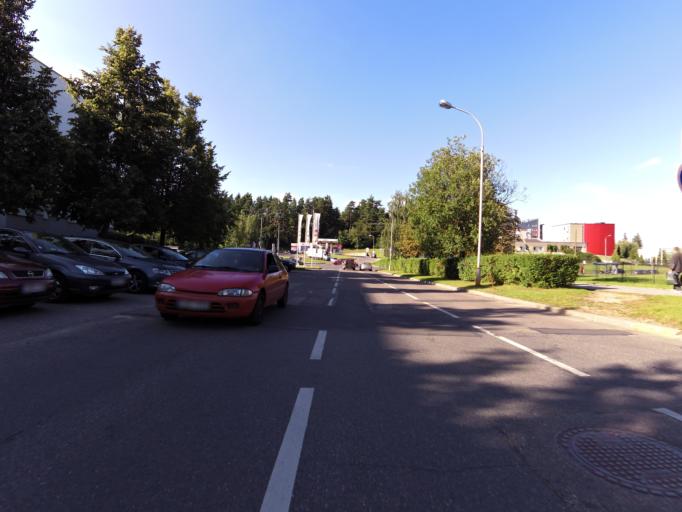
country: LT
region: Vilnius County
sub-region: Vilnius
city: Fabijoniskes
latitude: 54.7345
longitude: 25.2593
